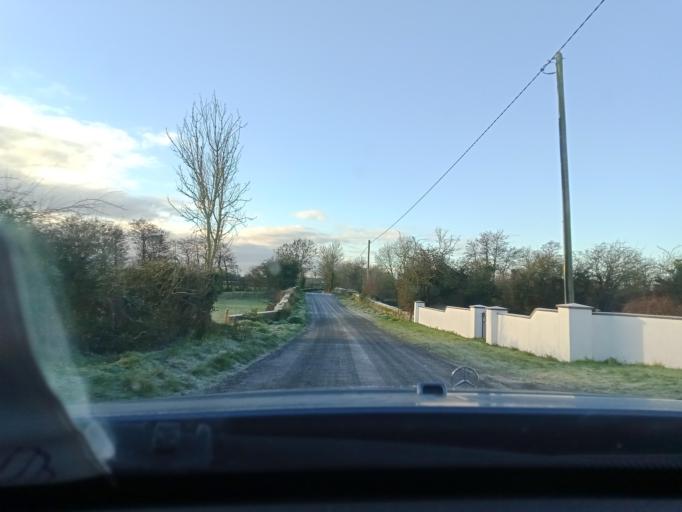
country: IE
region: Leinster
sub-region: County Carlow
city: Bagenalstown
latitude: 52.6468
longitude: -7.0038
